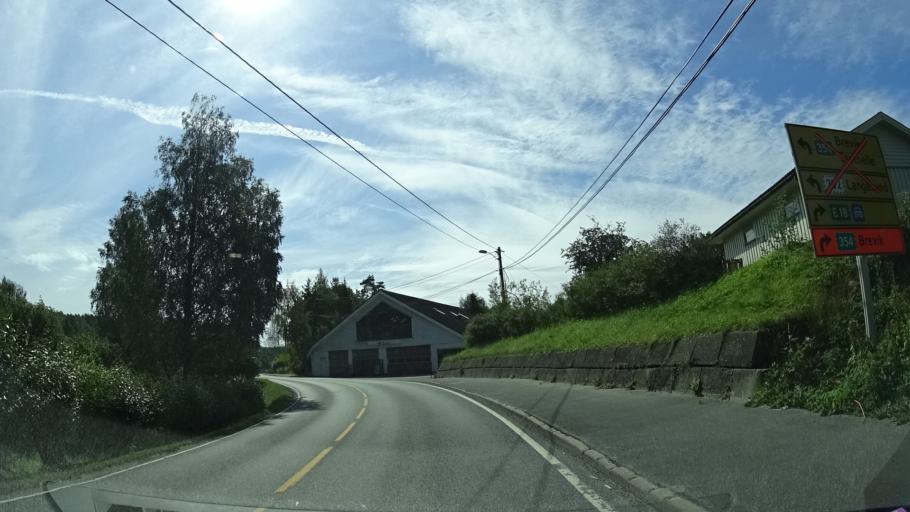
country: NO
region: Telemark
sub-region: Bamble
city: Langesund
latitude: 59.0419
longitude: 9.6723
